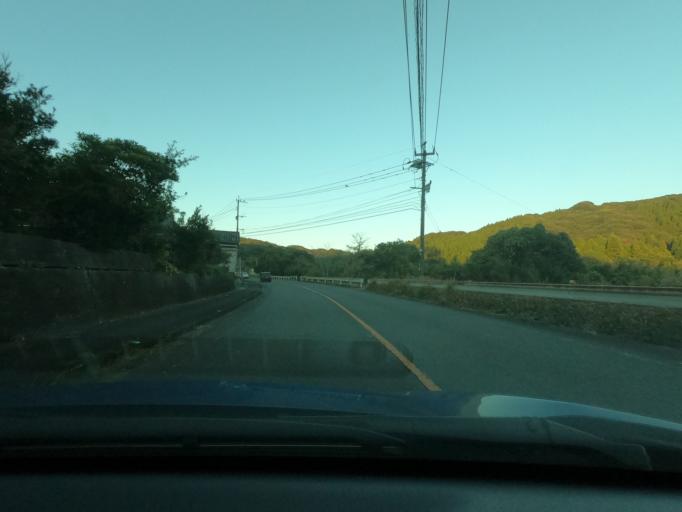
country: JP
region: Kagoshima
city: Satsumasendai
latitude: 31.7921
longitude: 130.4717
